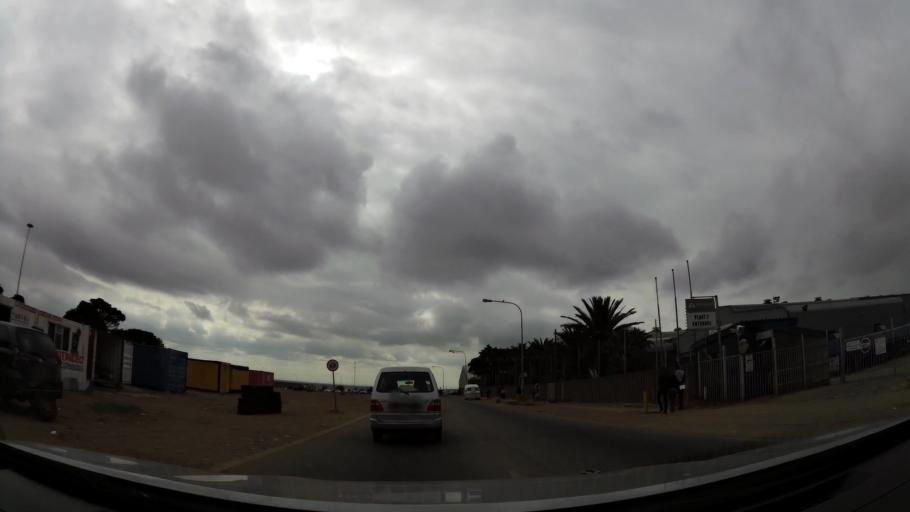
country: ZA
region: Eastern Cape
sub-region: Nelson Mandela Bay Metropolitan Municipality
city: Port Elizabeth
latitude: -33.8821
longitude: 25.5634
